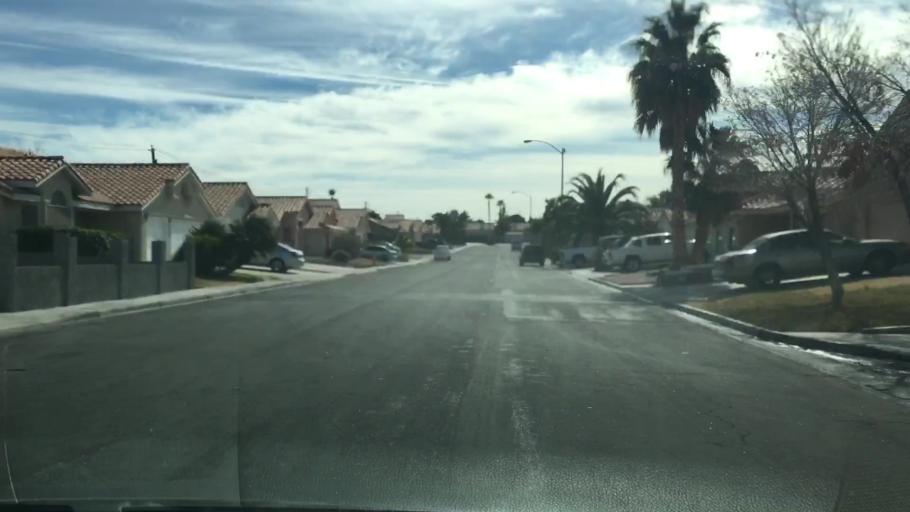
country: US
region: Nevada
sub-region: Clark County
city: Whitney
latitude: 36.0486
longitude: -115.1279
